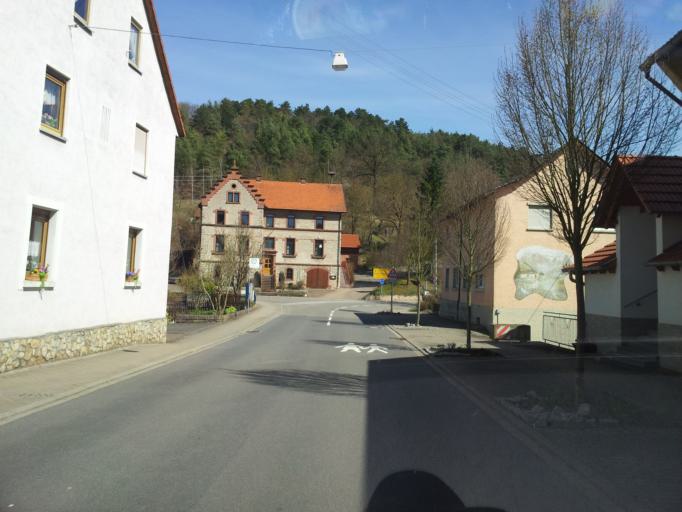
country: DE
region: Baden-Wuerttemberg
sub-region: Regierungsbezirk Stuttgart
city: Boxberg
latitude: 49.5267
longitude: 9.6212
